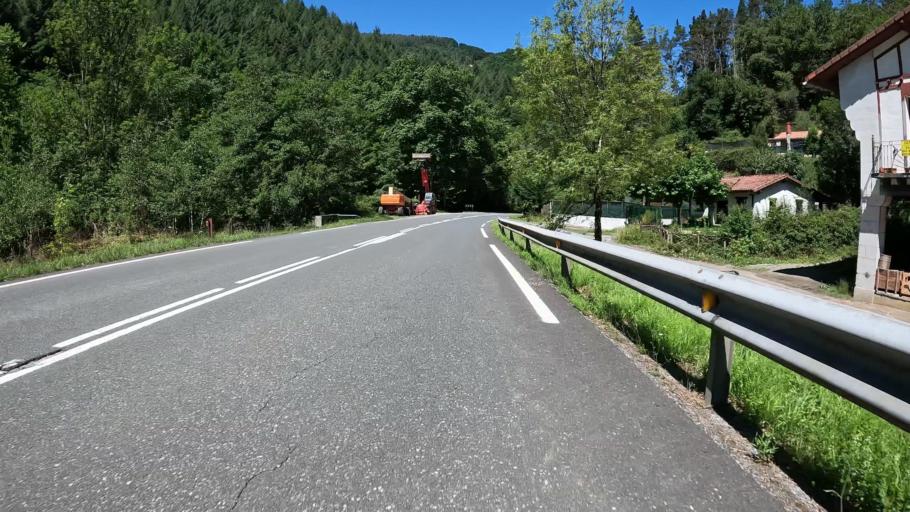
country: ES
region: Basque Country
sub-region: Provincia de Guipuzcoa
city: Oreja
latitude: 43.0750
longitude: -2.0146
